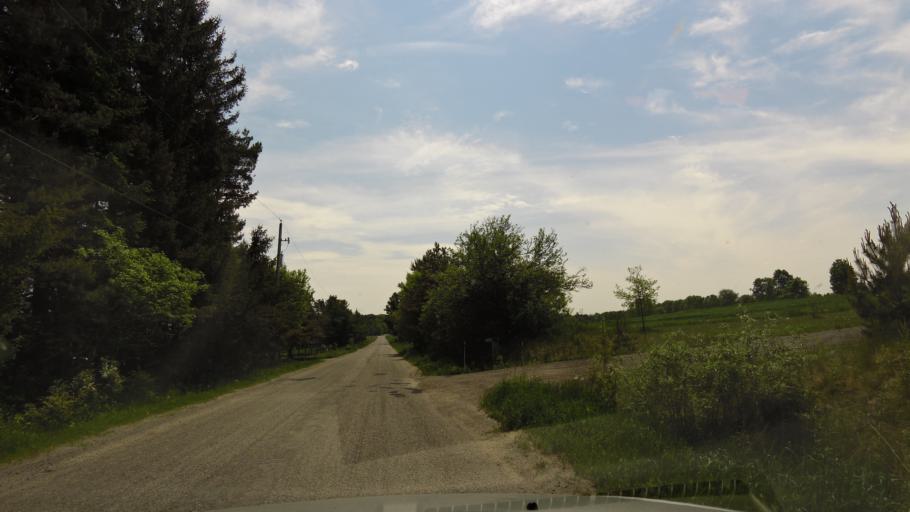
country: CA
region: Ontario
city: Cobourg
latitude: 43.9847
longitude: -78.4797
